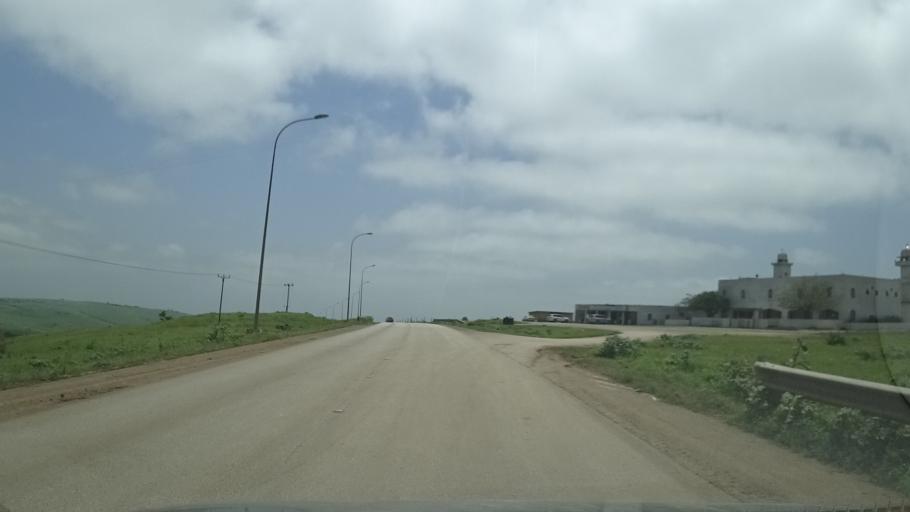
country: OM
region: Zufar
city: Salalah
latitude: 17.2130
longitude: 54.2474
